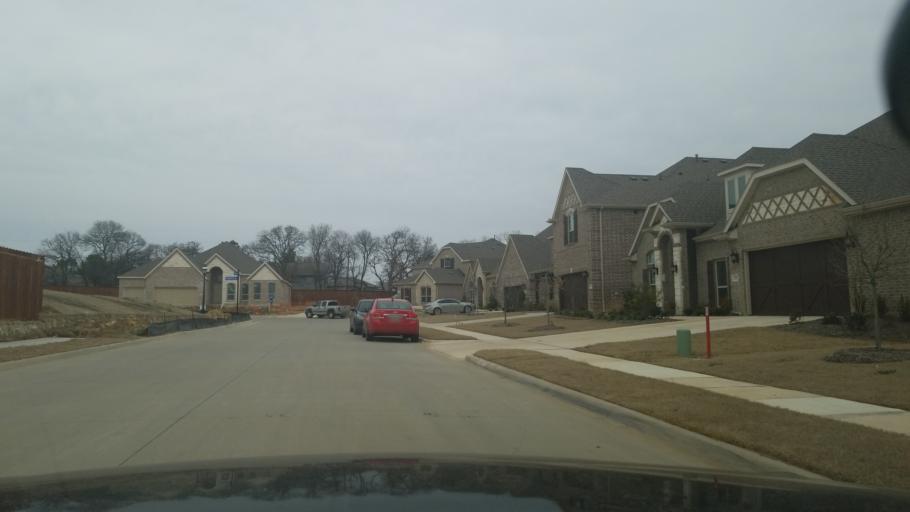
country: US
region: Texas
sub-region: Denton County
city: Corinth
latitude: 33.1346
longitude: -97.0770
